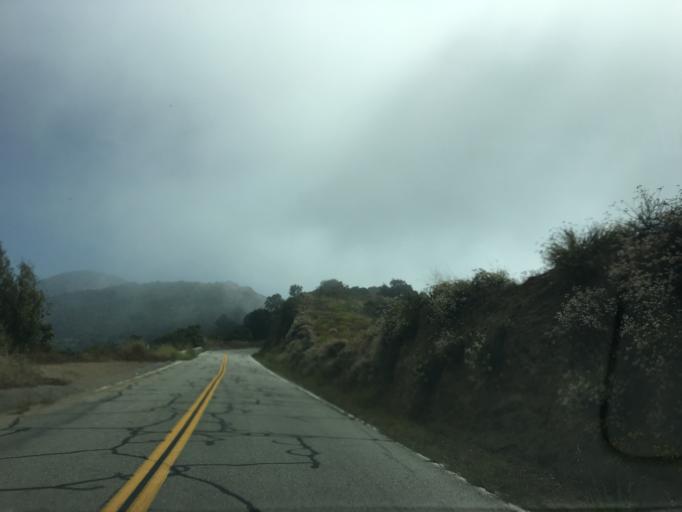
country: US
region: California
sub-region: Los Angeles County
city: Glendora
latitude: 34.1787
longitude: -117.8456
